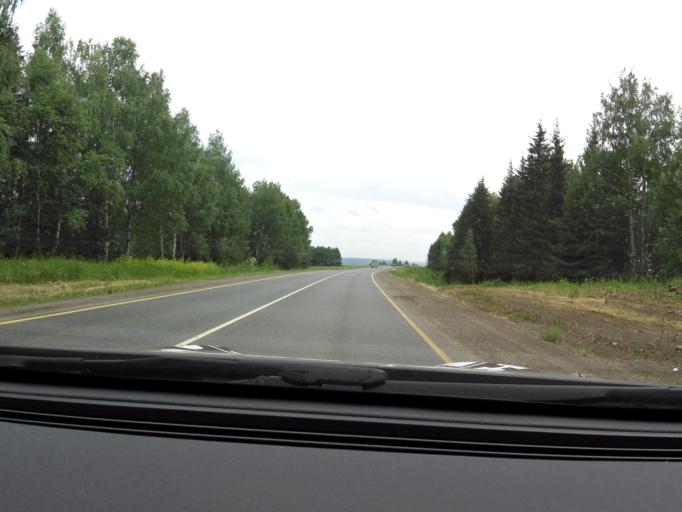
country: RU
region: Perm
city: Kungur
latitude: 57.4770
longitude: 56.7283
